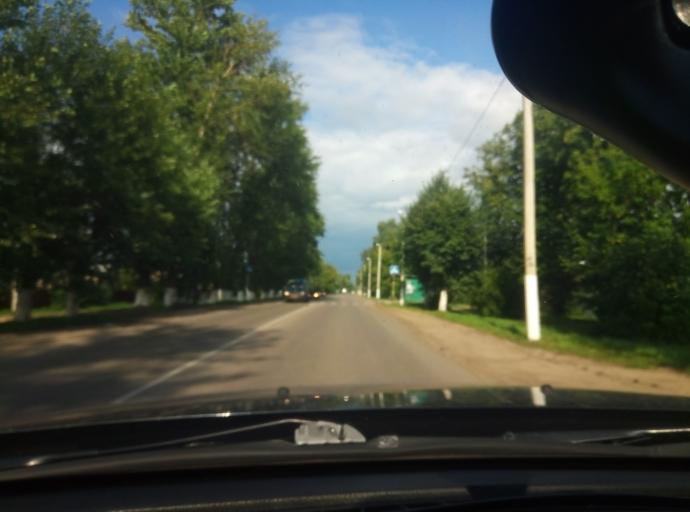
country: RU
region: Tula
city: Donskoy
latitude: 53.9684
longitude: 38.3498
